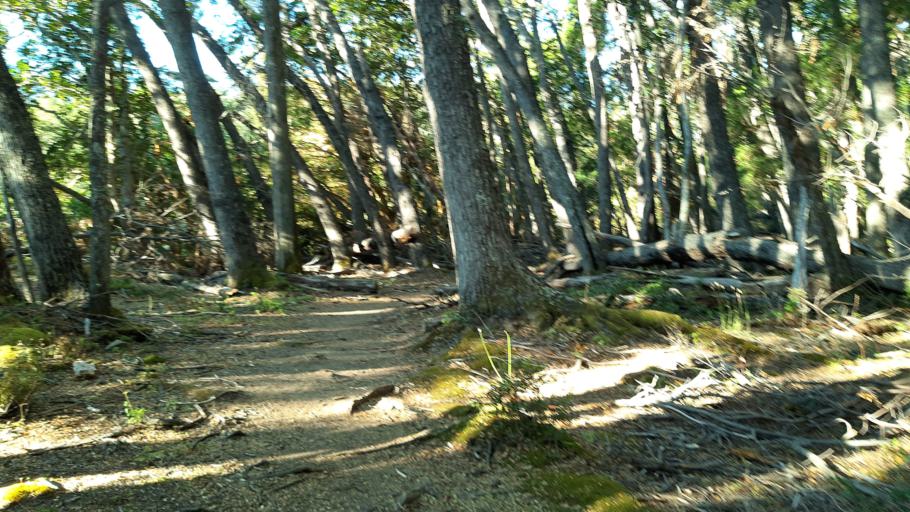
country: AR
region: Chubut
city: Trevelin
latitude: -42.7462
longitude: -71.7475
